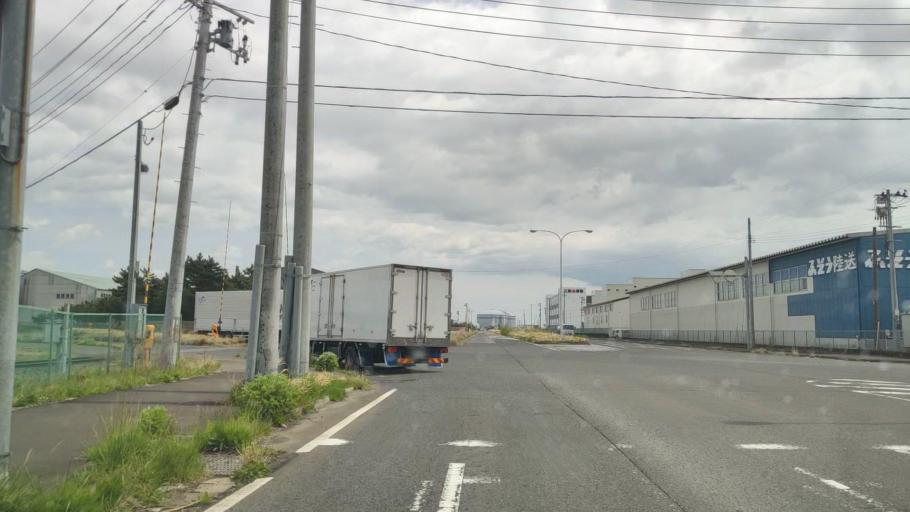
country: JP
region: Miyagi
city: Shiogama
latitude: 38.2761
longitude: 141.0170
